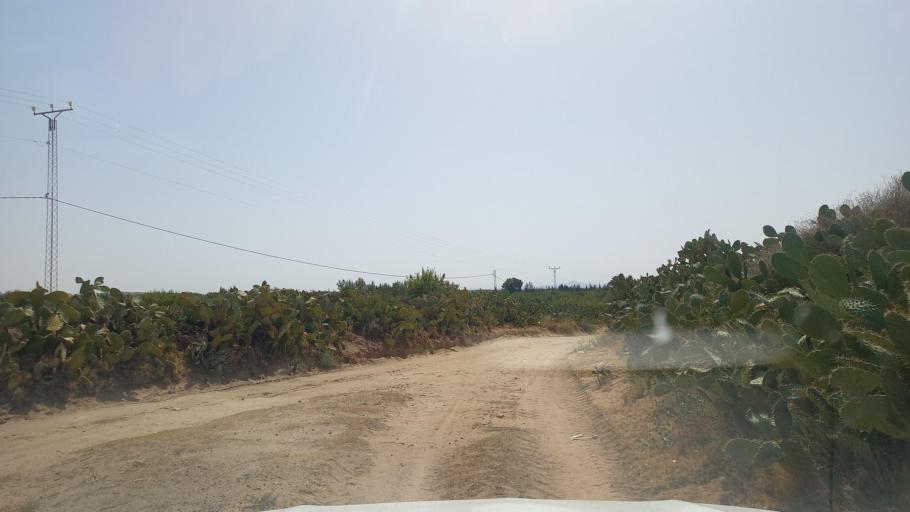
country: TN
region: Al Qasrayn
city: Kasserine
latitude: 35.2404
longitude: 9.0697
